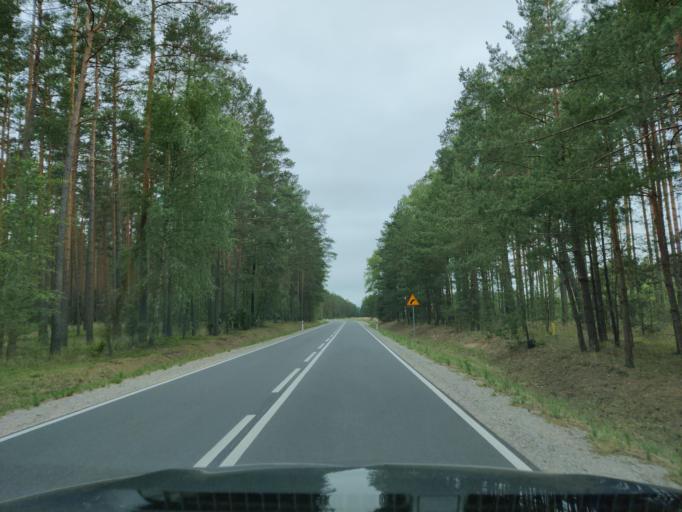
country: PL
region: Masovian Voivodeship
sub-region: Powiat ostrolecki
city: Czarnia
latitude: 53.3452
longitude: 21.2393
